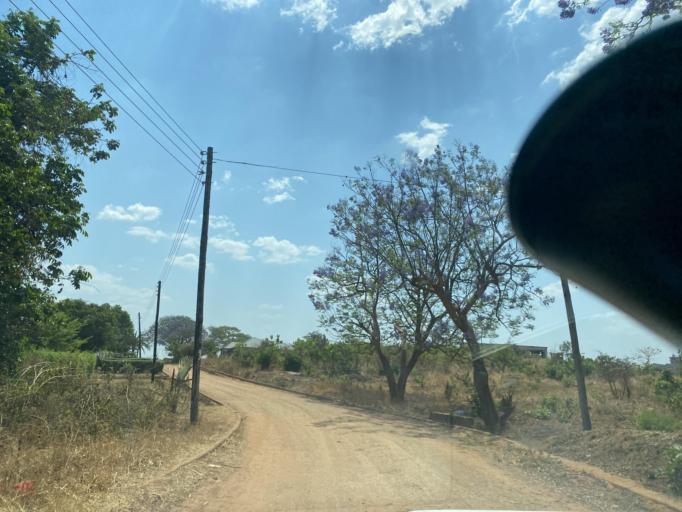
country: ZM
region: Lusaka
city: Kafue
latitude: -15.5053
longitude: 27.9343
